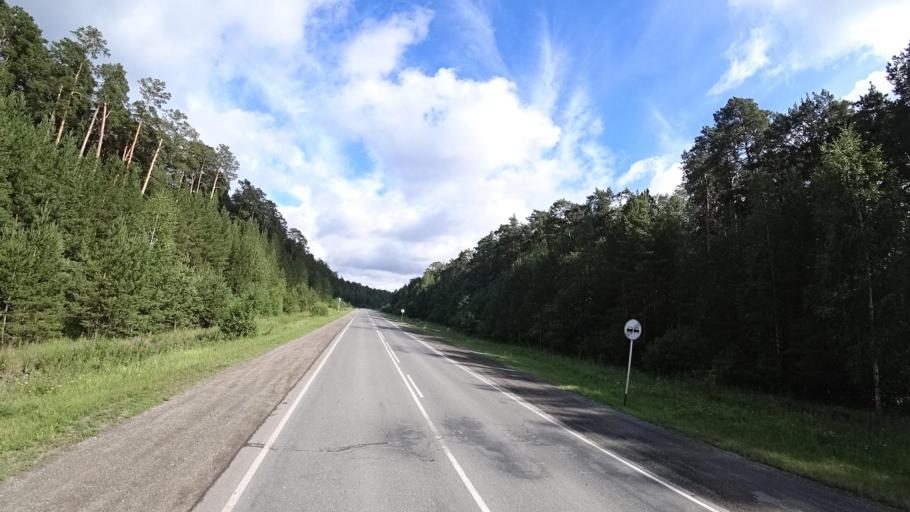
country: RU
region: Sverdlovsk
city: Kamyshlov
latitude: 56.8257
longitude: 62.7017
